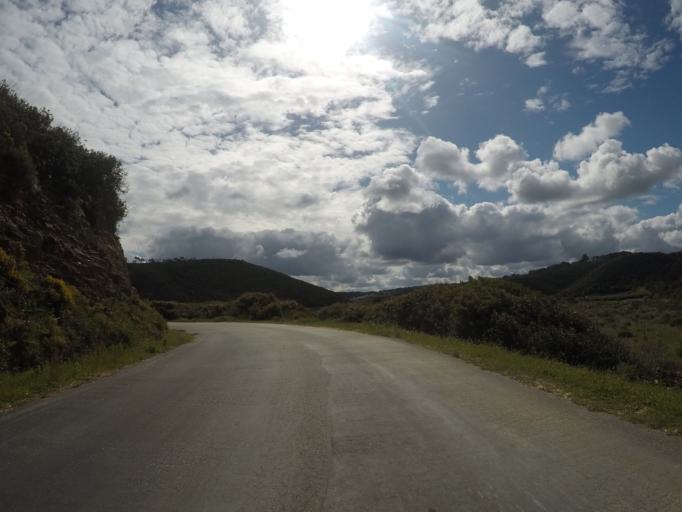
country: PT
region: Beja
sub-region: Odemira
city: Sao Teotonio
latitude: 37.4372
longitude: -8.7913
